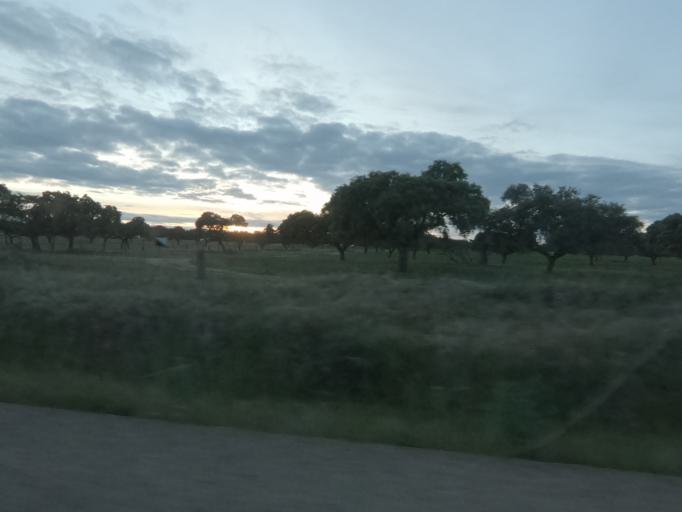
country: ES
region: Extremadura
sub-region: Provincia de Badajoz
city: Badajoz
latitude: 38.9583
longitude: -6.9049
